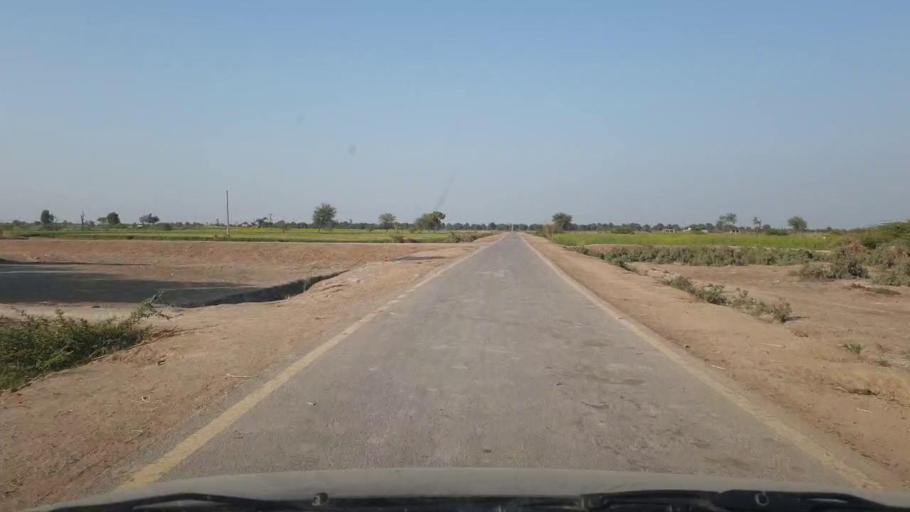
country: PK
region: Sindh
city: Samaro
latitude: 25.2903
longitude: 69.3486
